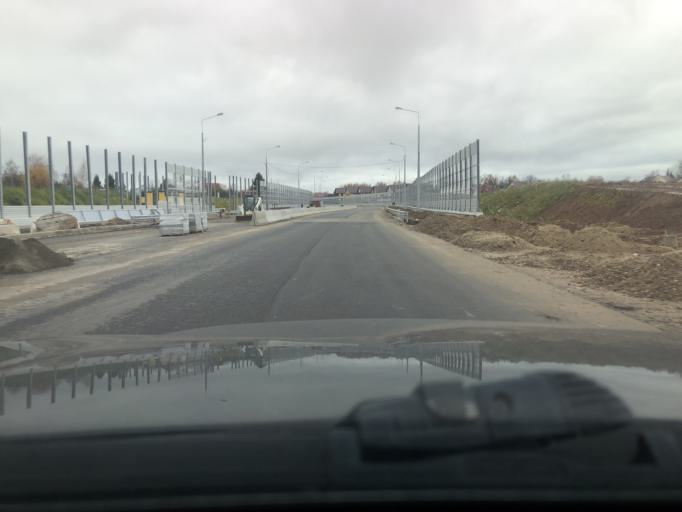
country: RU
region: Moskovskaya
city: Sergiyev Posad
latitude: 56.3014
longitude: 38.1004
